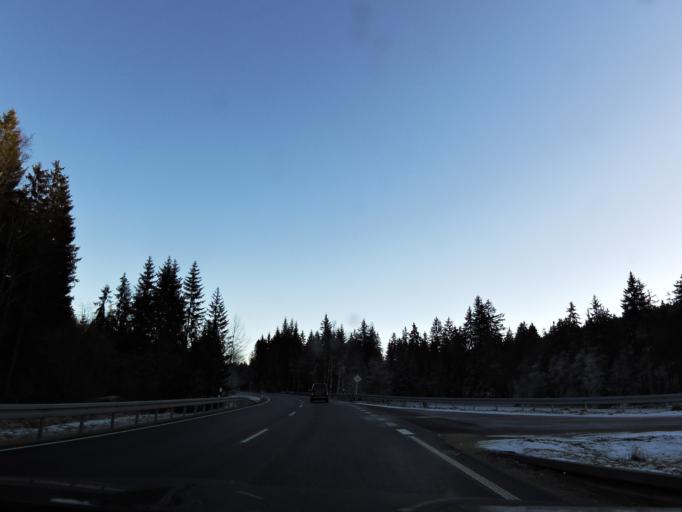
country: DE
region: Bavaria
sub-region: Upper Franconia
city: Fichtelberg
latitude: 50.0374
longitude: 11.8399
